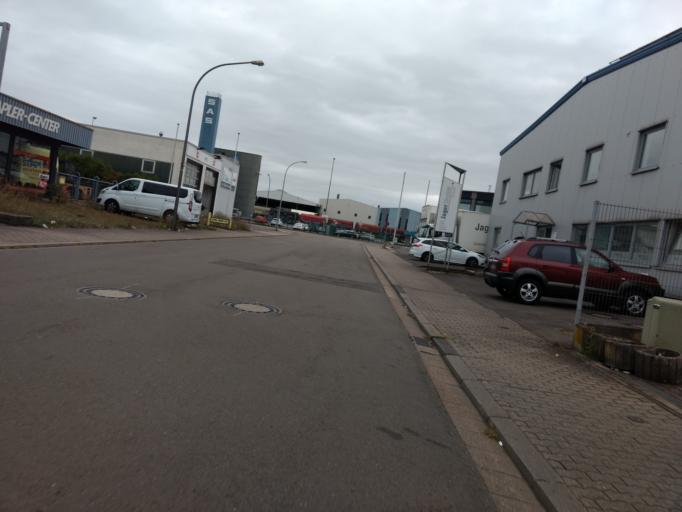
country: DE
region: Saarland
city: Dillingen
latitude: 49.3444
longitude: 6.7466
